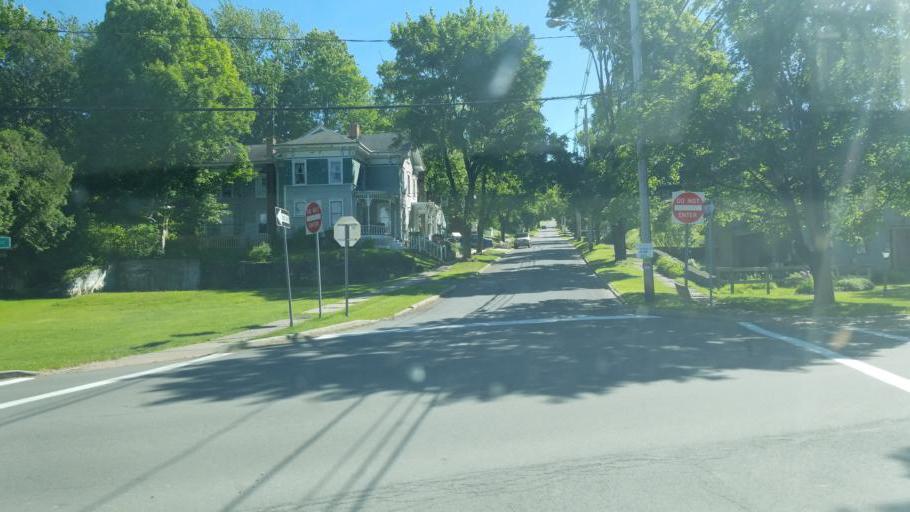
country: US
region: New York
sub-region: Montgomery County
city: Canajoharie
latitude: 42.9026
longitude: -74.5761
